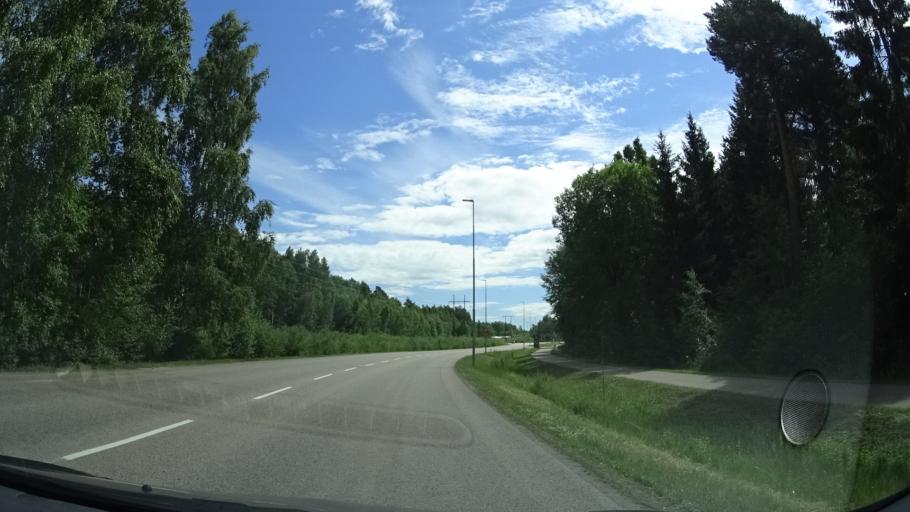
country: SE
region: Vaestmanland
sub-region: Vasteras
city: Hokasen
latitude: 59.6431
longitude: 16.5866
